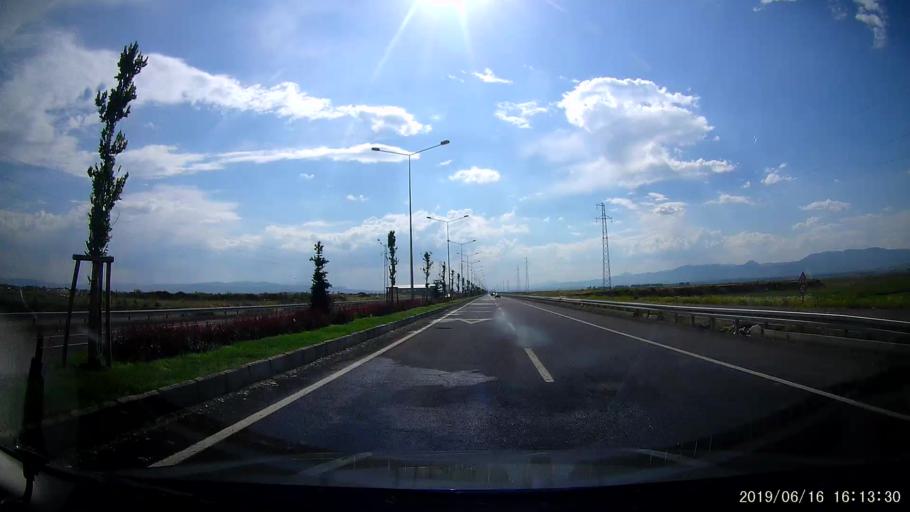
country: TR
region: Erzurum
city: Erzurum
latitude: 39.9596
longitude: 41.2708
